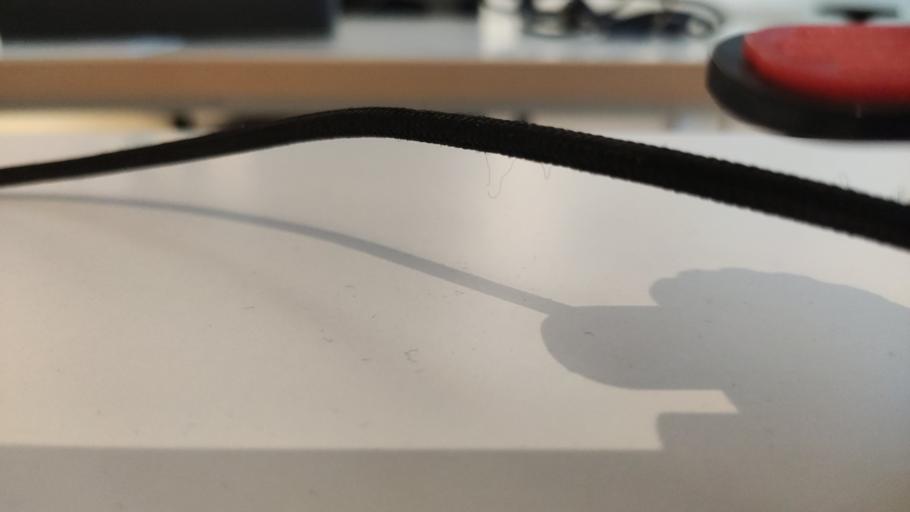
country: RU
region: Moskovskaya
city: Novopetrovskoye
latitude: 55.8599
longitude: 36.3827
